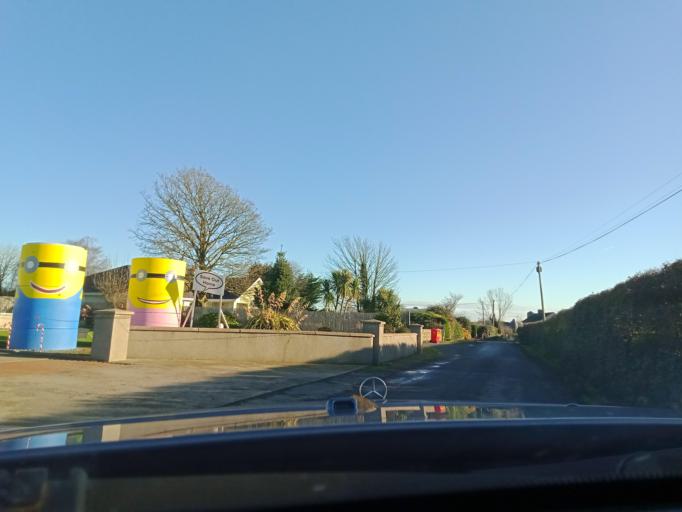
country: IE
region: Leinster
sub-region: Kilkenny
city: Mooncoin
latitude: 52.2898
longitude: -7.2106
